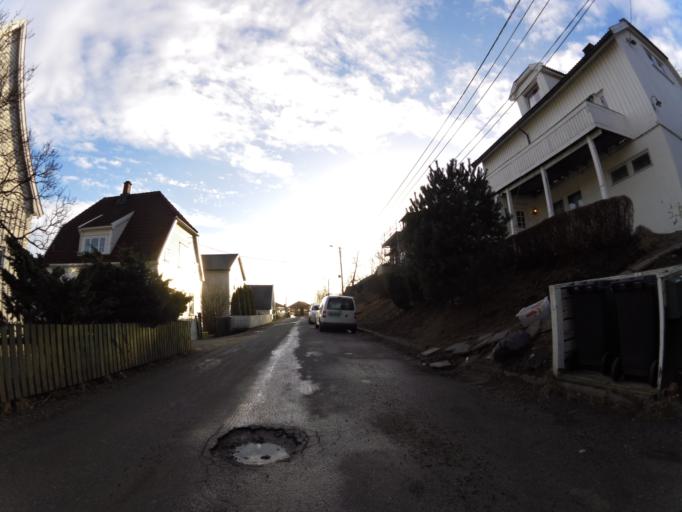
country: NO
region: Ostfold
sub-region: Fredrikstad
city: Fredrikstad
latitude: 59.2208
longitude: 10.9474
